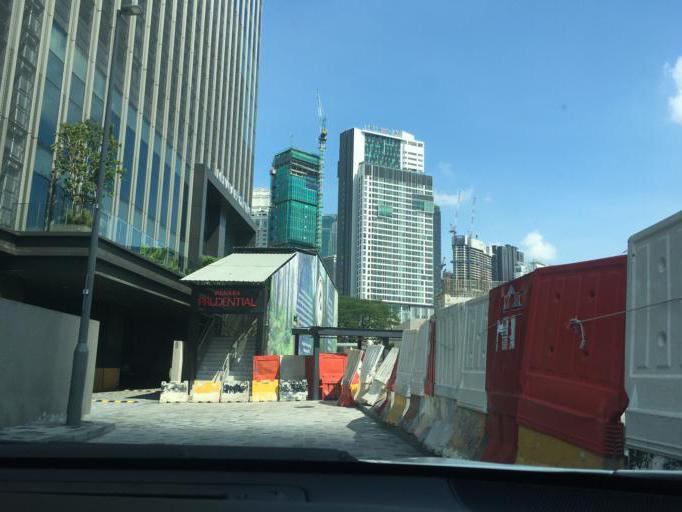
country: MY
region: Kuala Lumpur
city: Kuala Lumpur
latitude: 3.1433
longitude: 101.7163
